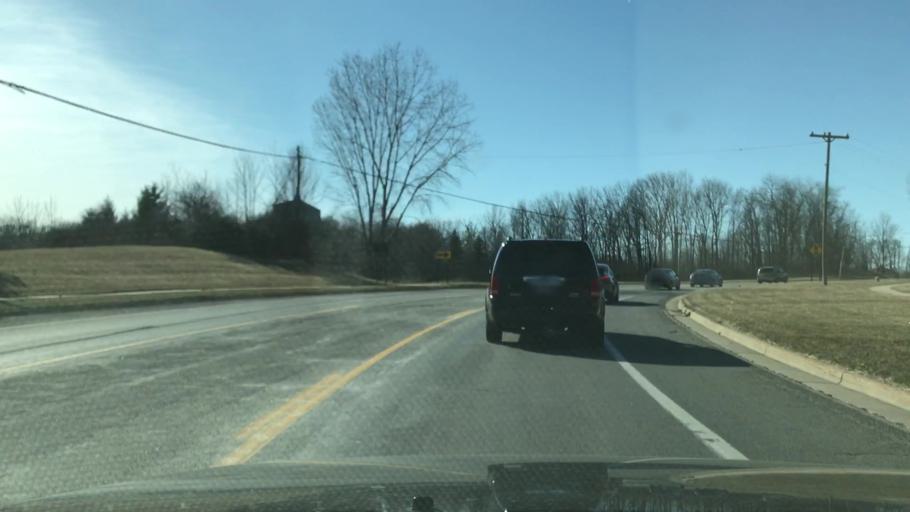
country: US
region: Michigan
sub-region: Kent County
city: East Grand Rapids
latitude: 42.9198
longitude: -85.5562
